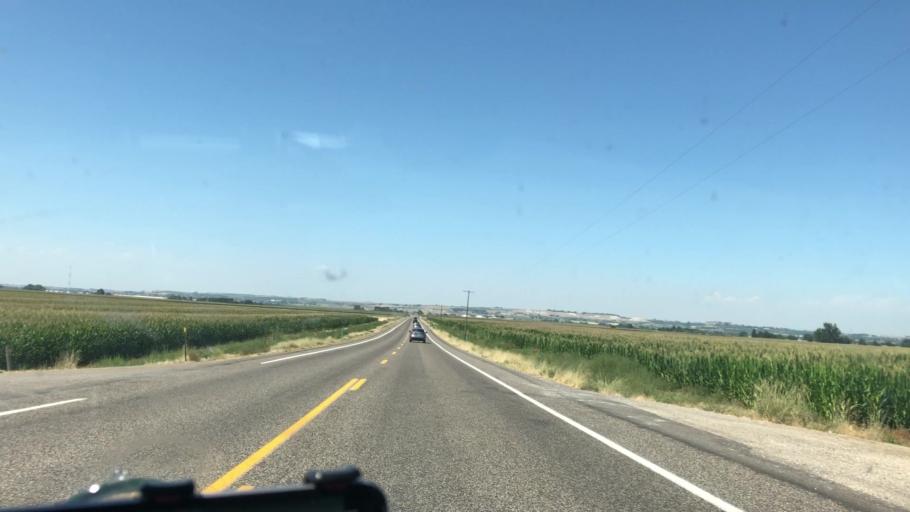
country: US
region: Idaho
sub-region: Owyhee County
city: Marsing
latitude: 43.5234
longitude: -116.8515
